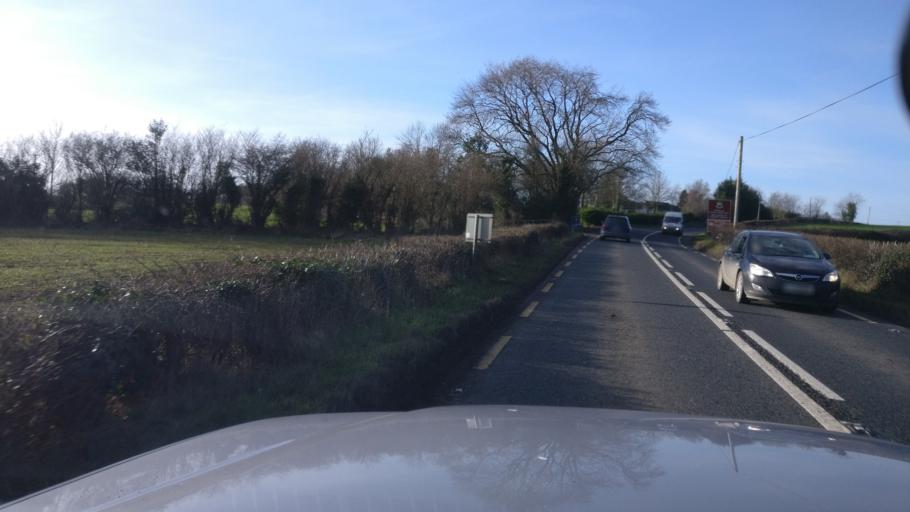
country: IE
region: Leinster
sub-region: Uibh Fhaili
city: Tullamore
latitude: 53.1990
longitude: -7.4276
